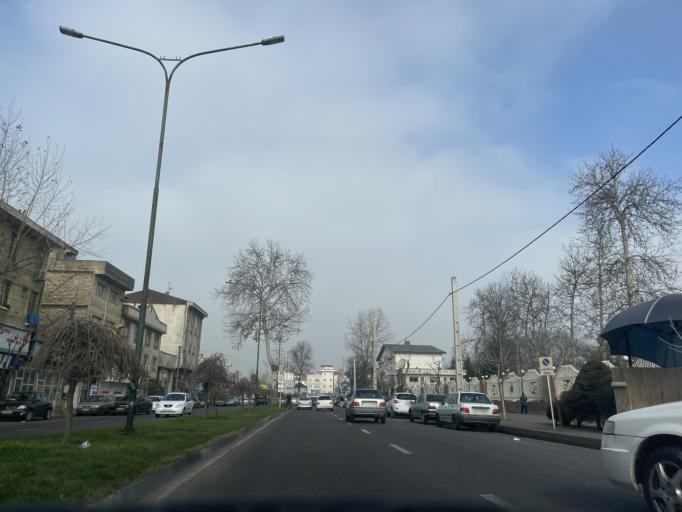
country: IR
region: Gilan
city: Rasht
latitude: 37.2736
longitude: 49.6084
